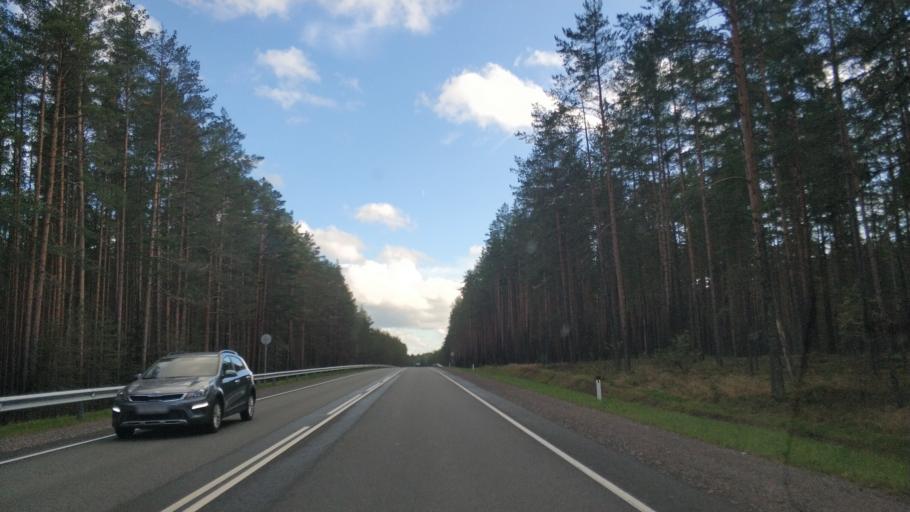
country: RU
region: Leningrad
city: Priozersk
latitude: 60.9915
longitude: 30.1833
